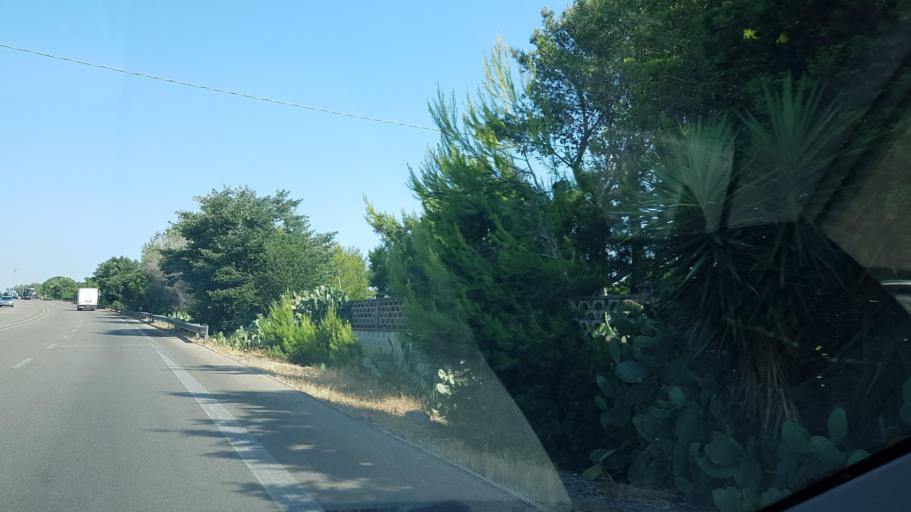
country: IT
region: Apulia
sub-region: Provincia di Lecce
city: Maglie
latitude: 40.1194
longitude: 18.3194
